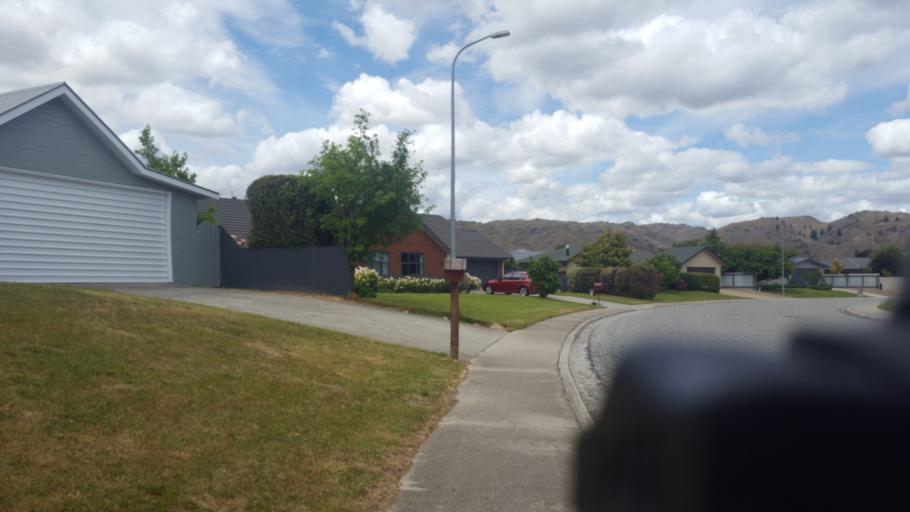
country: NZ
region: Otago
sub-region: Queenstown-Lakes District
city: Wanaka
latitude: -45.2537
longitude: 169.3846
